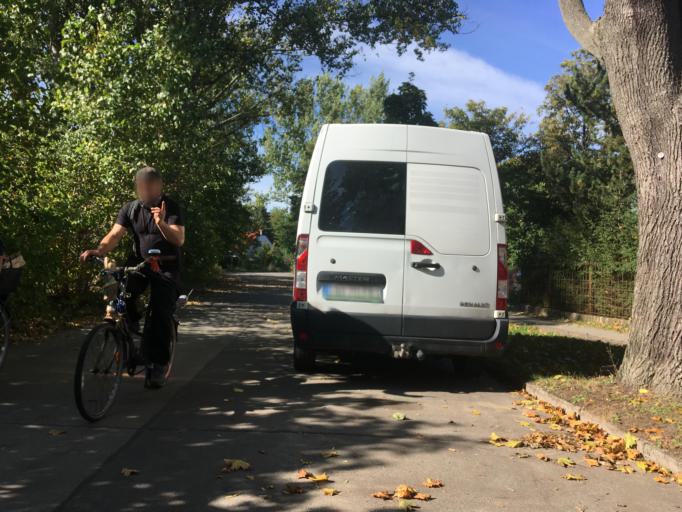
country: DE
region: Berlin
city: Altglienicke
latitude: 52.4091
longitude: 13.5535
